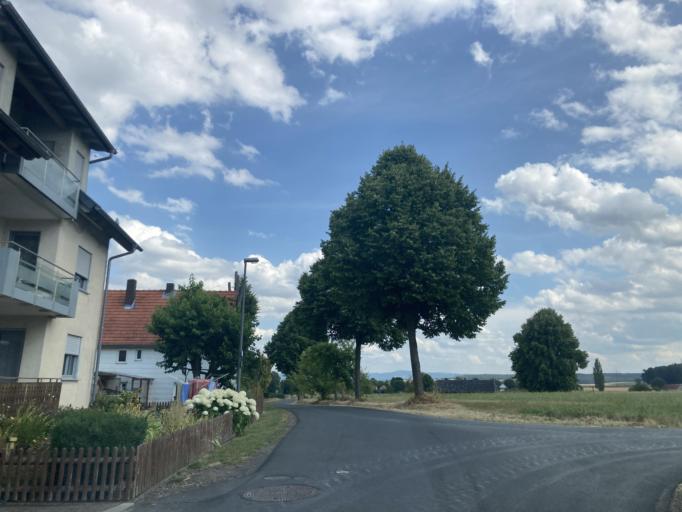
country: DE
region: Hesse
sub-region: Regierungsbezirk Kassel
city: Fulda
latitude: 50.5317
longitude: 9.6134
